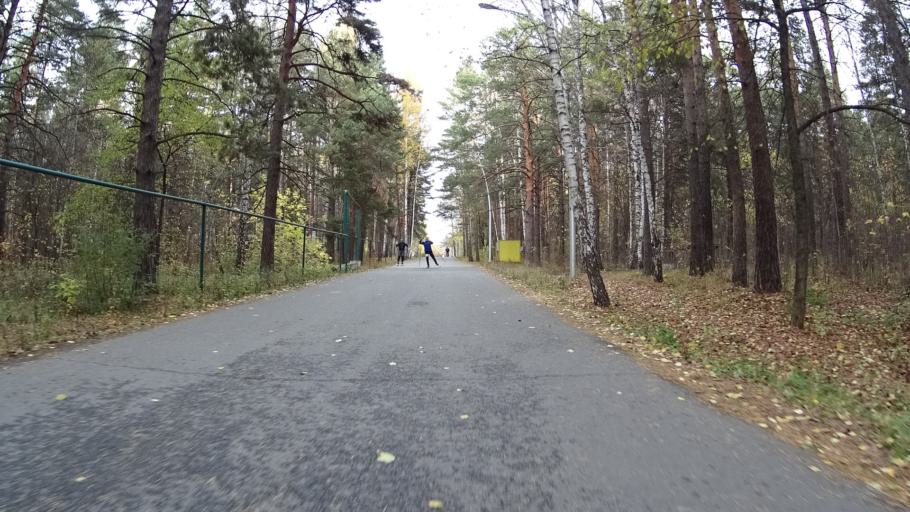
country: RU
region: Chelyabinsk
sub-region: Gorod Chelyabinsk
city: Chelyabinsk
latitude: 55.1447
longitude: 61.3521
